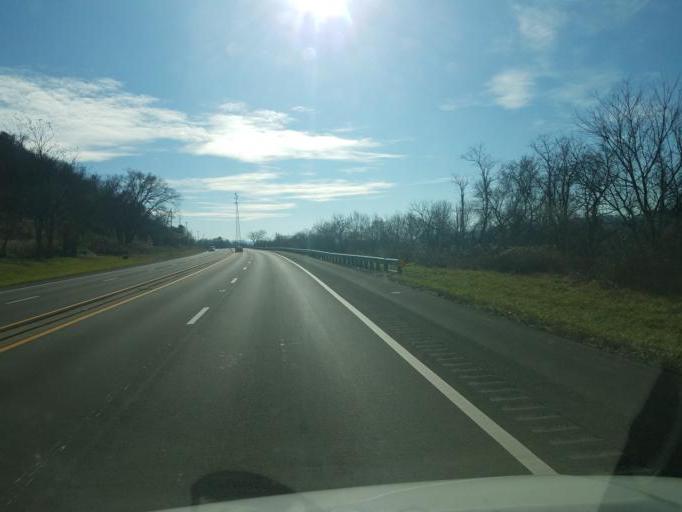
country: US
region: Ohio
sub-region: Scioto County
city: Rosemount
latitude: 38.8003
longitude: -82.9847
